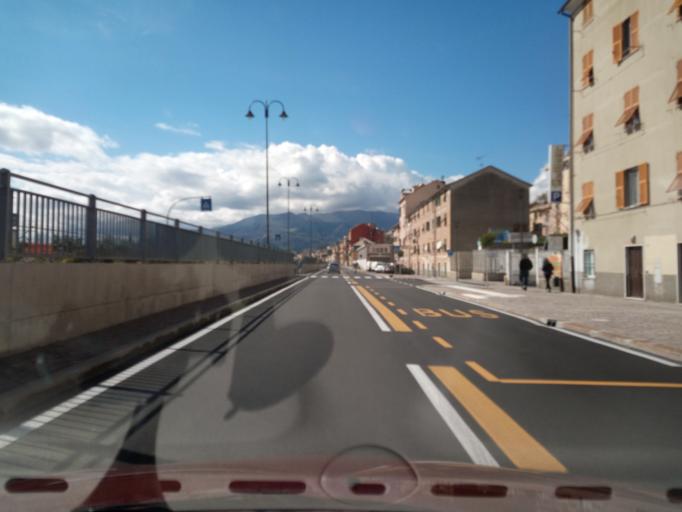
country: IT
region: Liguria
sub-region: Provincia di Genova
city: Mele
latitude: 44.4258
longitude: 8.7940
